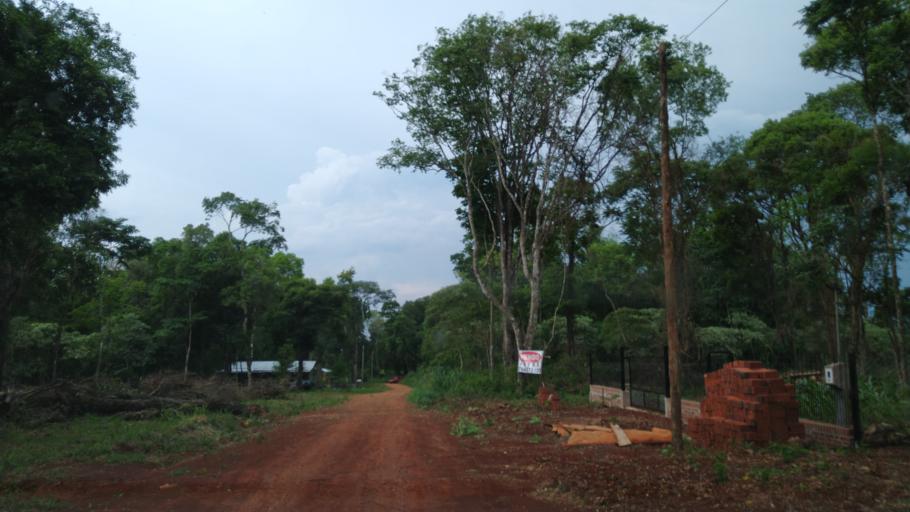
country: AR
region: Misiones
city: Capiovi
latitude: -26.9326
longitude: -55.0492
